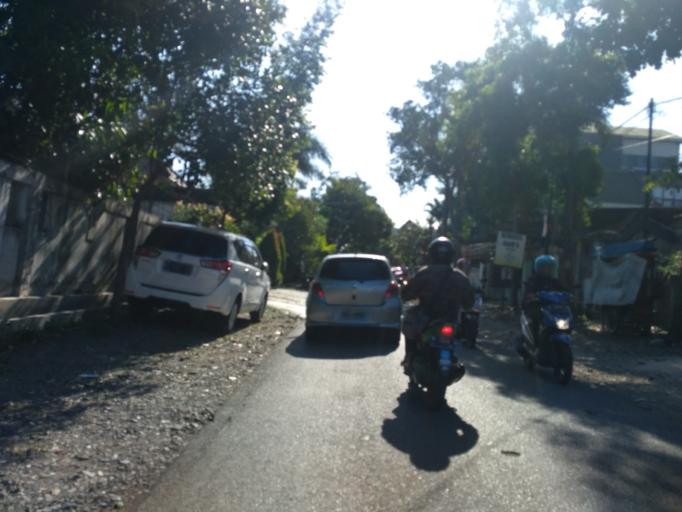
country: ID
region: East Java
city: Malang
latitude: -7.9401
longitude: 112.6261
